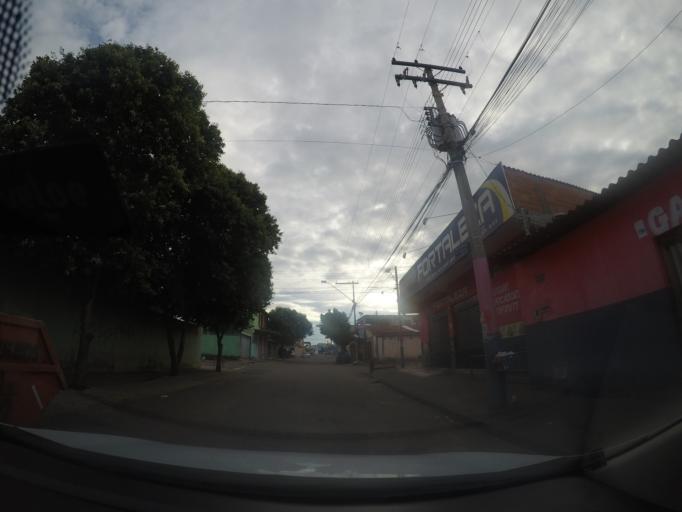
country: BR
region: Goias
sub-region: Goiania
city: Goiania
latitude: -16.6428
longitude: -49.3222
